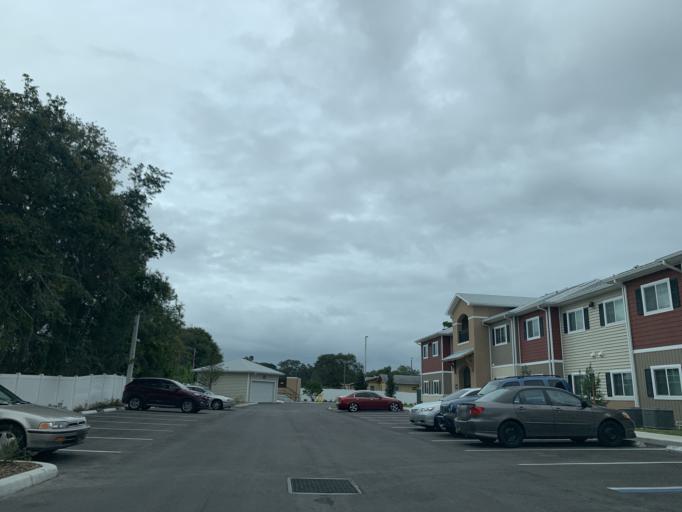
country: US
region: Florida
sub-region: Pinellas County
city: Belleair
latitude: 27.9443
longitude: -82.7948
